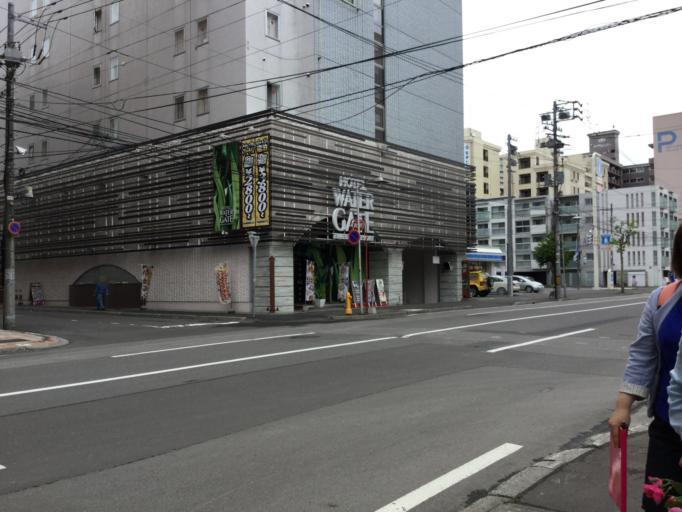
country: JP
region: Hokkaido
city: Sapporo
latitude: 43.0530
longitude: 141.3474
